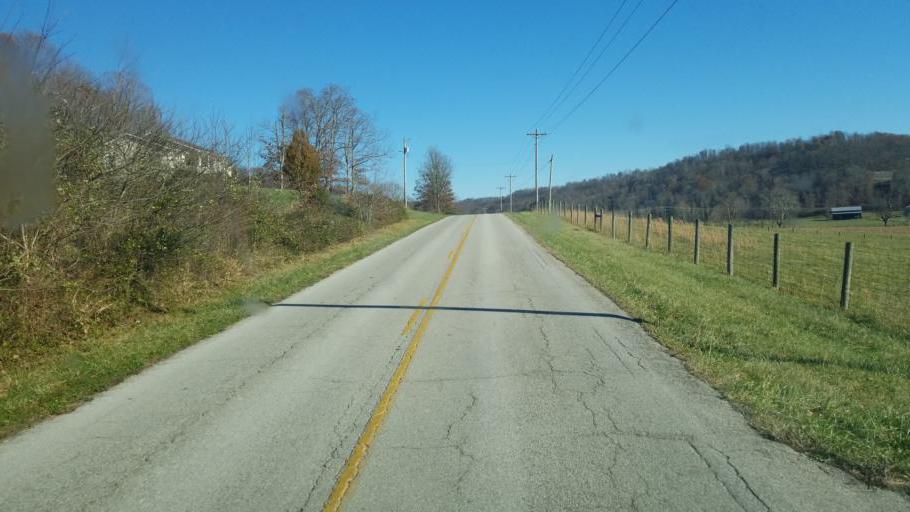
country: US
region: Kentucky
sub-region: Fleming County
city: Flemingsburg
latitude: 38.4684
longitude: -83.5436
